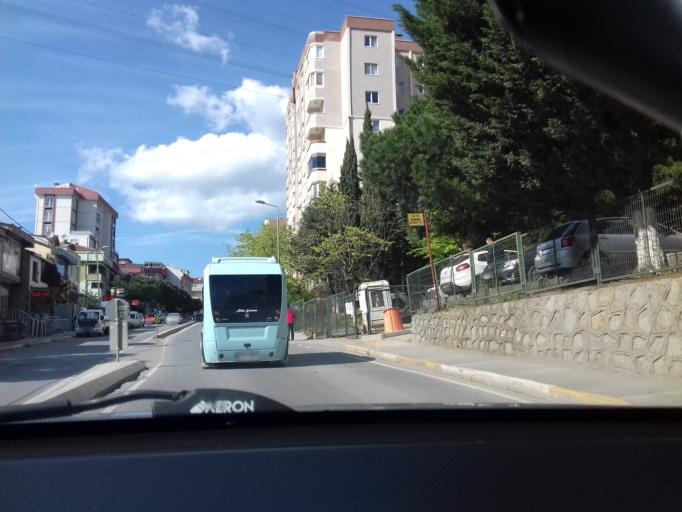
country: TR
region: Istanbul
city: Pendik
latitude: 40.9113
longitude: 29.2825
